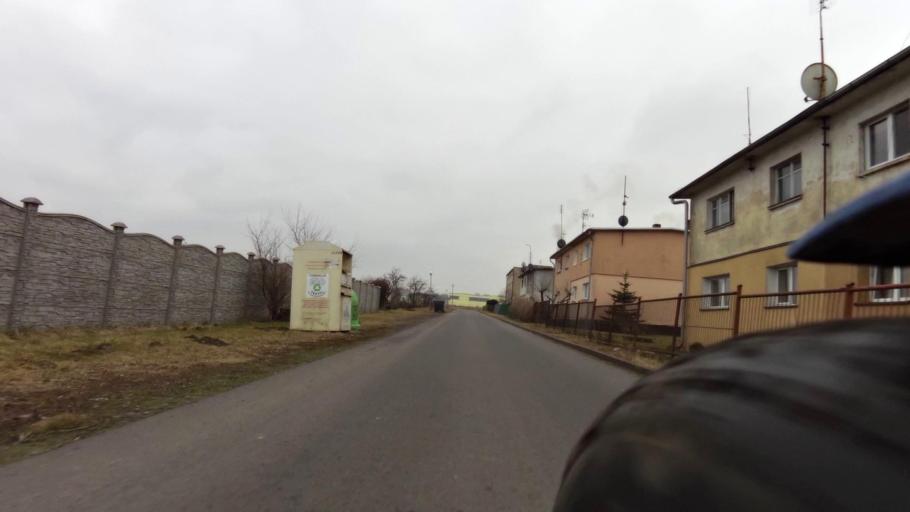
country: PL
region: West Pomeranian Voivodeship
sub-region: Powiat walecki
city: Walcz
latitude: 53.2286
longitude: 16.4538
